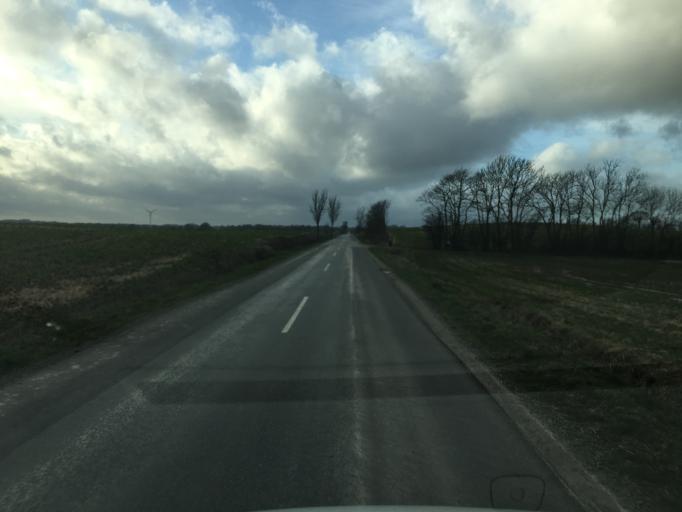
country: DK
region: South Denmark
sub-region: Sonderborg Kommune
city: Grasten
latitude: 54.9634
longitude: 9.5414
